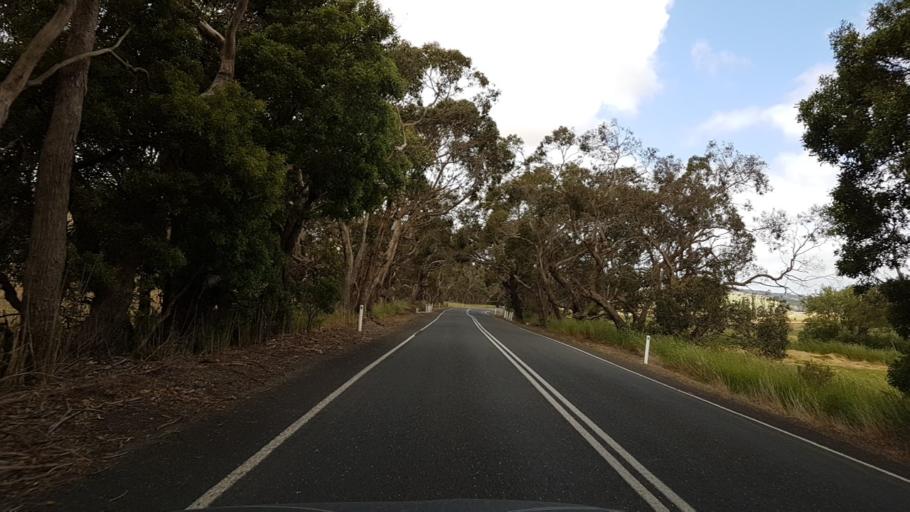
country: AU
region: South Australia
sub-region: Alexandrina
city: Mount Compass
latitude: -35.4092
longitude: 138.5384
